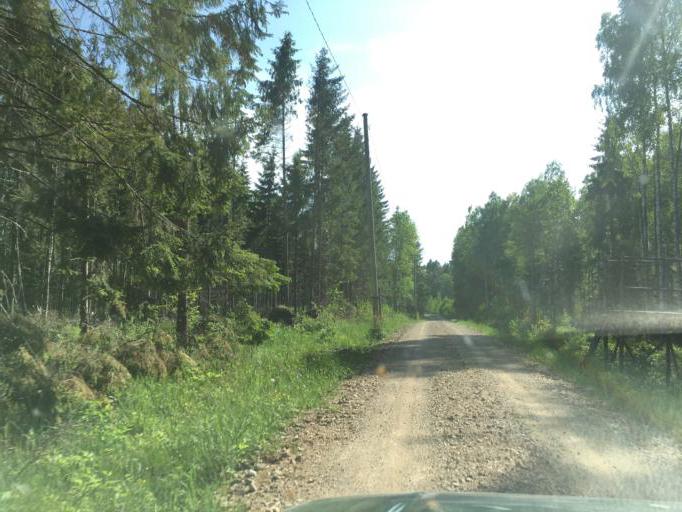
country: LV
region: Dundaga
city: Dundaga
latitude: 57.6064
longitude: 22.5131
